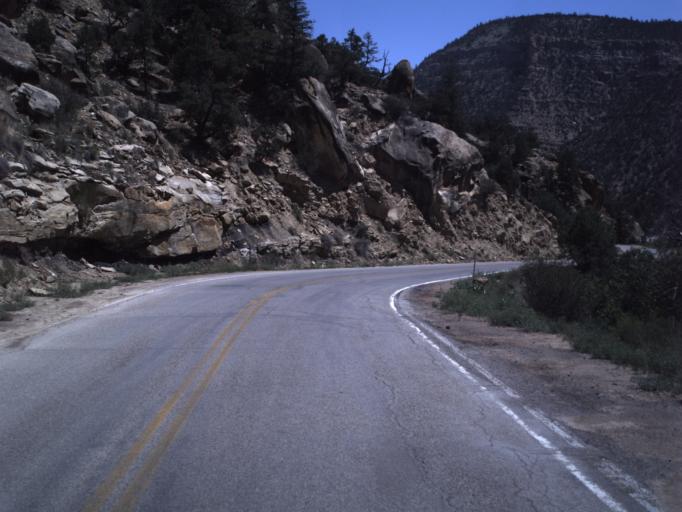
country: US
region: Utah
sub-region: Emery County
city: Orangeville
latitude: 39.2796
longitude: -111.2287
